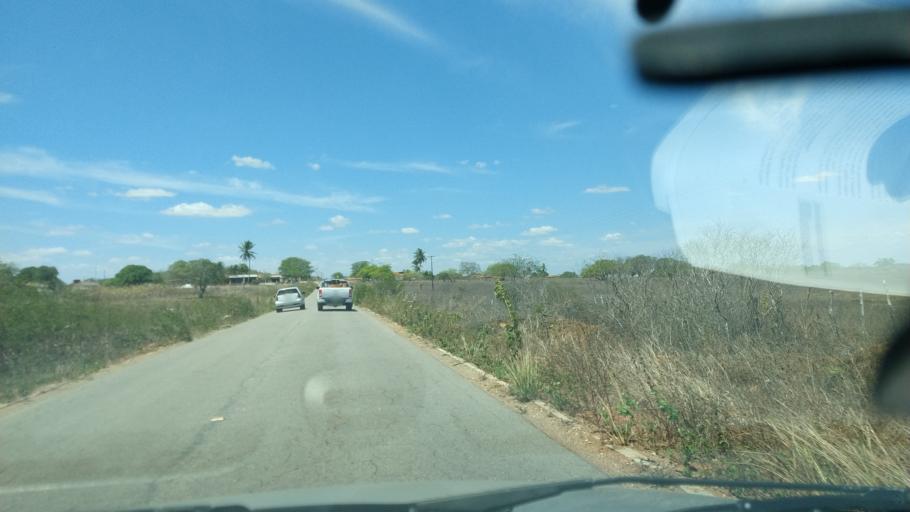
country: BR
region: Rio Grande do Norte
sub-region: Sao Paulo Do Potengi
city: Sao Paulo do Potengi
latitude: -5.9202
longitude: -35.5822
